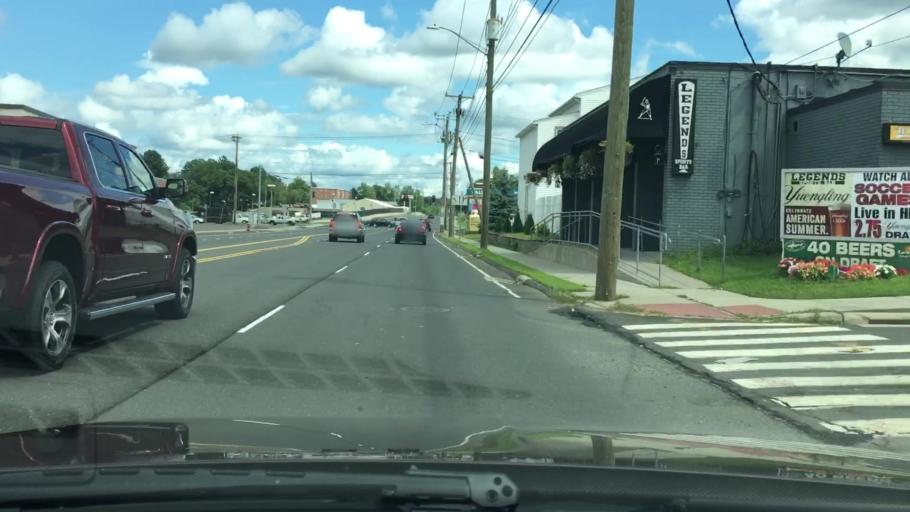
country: US
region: Connecticut
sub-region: Hartford County
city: Bristol
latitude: 41.6682
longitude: -72.9155
